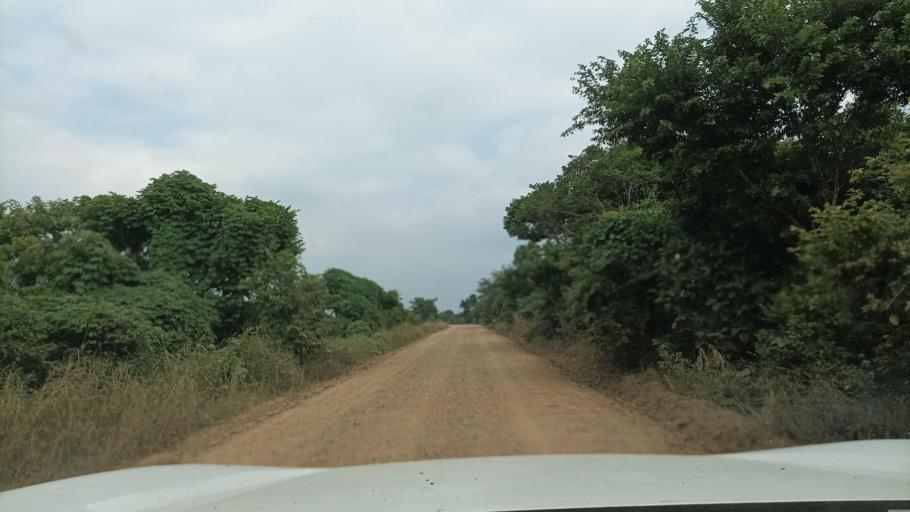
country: MX
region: Veracruz
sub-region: Texistepec
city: San Lorenzo Tenochtitlan
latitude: 17.7766
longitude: -94.7957
